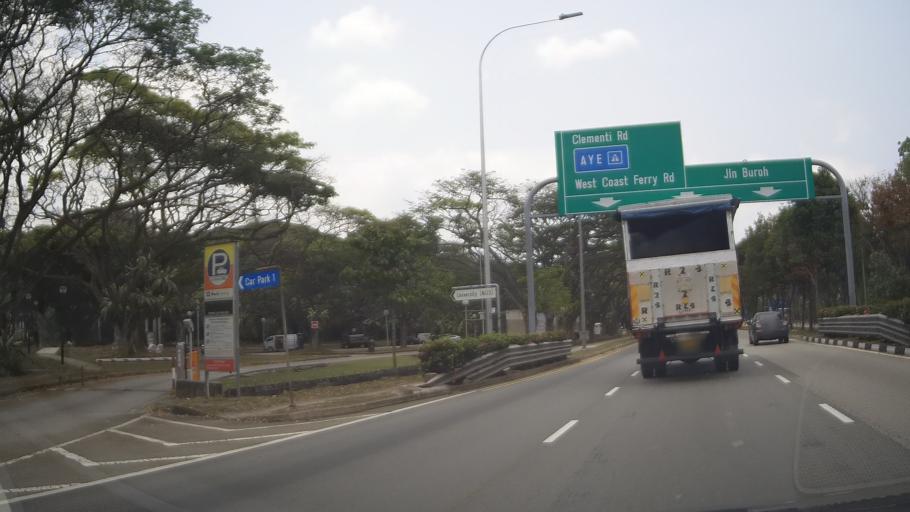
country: SG
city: Singapore
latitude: 1.2896
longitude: 103.7724
